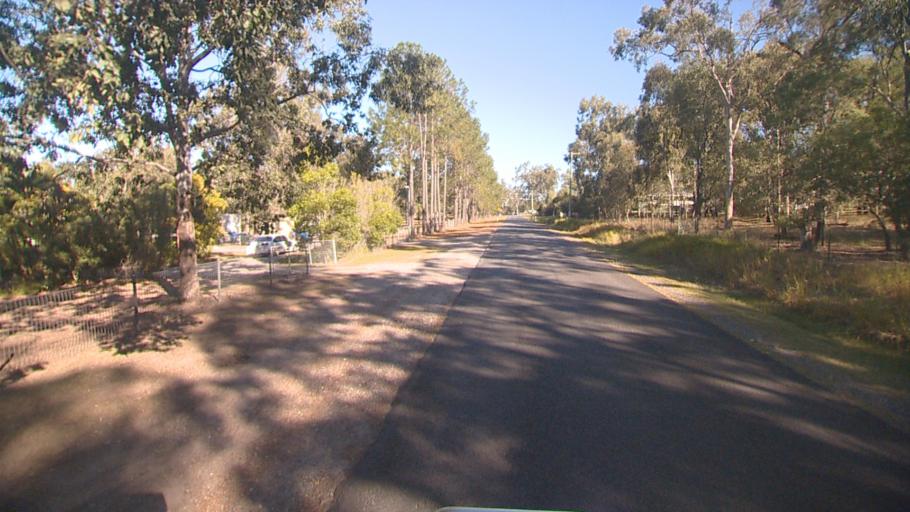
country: AU
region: Queensland
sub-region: Logan
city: Park Ridge South
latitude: -27.7343
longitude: 153.0218
